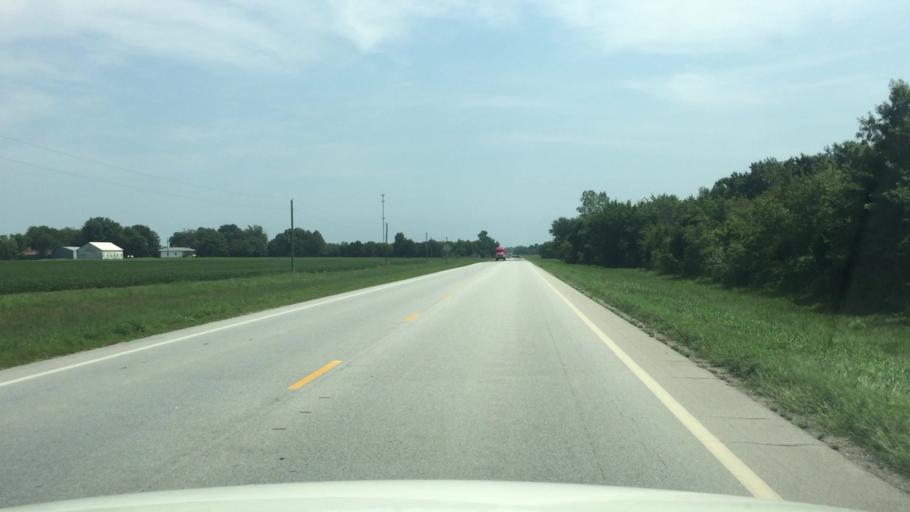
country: US
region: Kansas
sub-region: Cherokee County
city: Columbus
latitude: 37.1787
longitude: -94.8661
